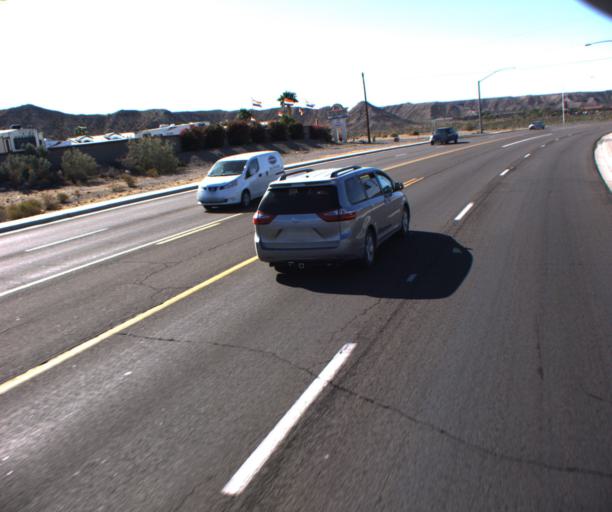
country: US
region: Arizona
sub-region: Mohave County
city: Bullhead City
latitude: 35.0706
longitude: -114.5897
